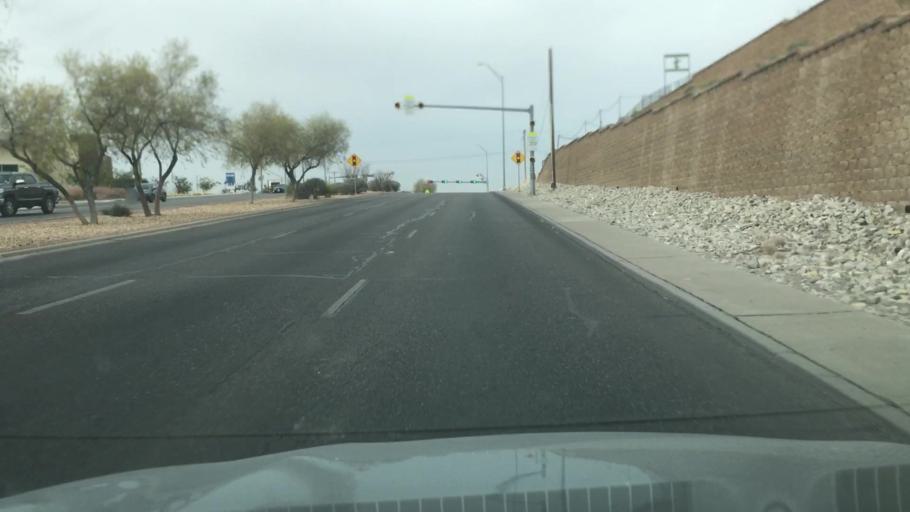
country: US
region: New Mexico
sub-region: Dona Ana County
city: Sunland Park
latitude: 31.8347
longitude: -106.5448
